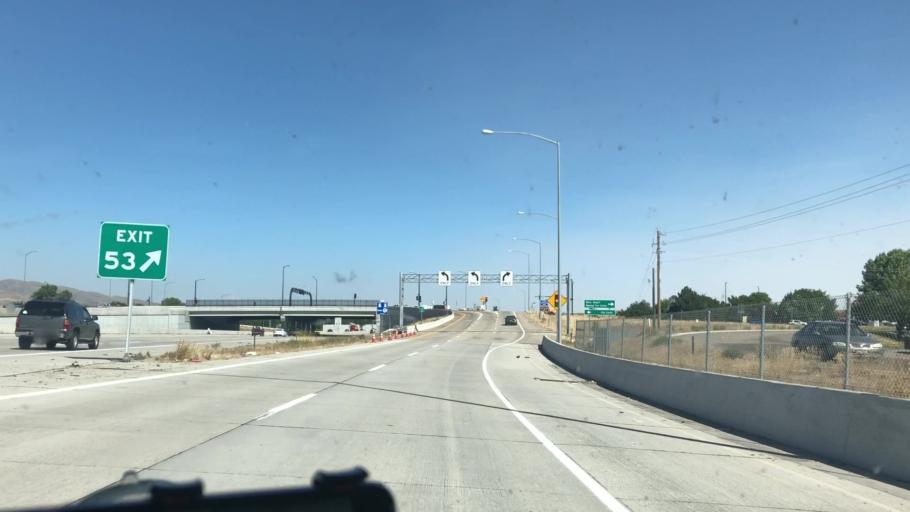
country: US
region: Idaho
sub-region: Ada County
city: Boise
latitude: 43.5716
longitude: -116.2189
